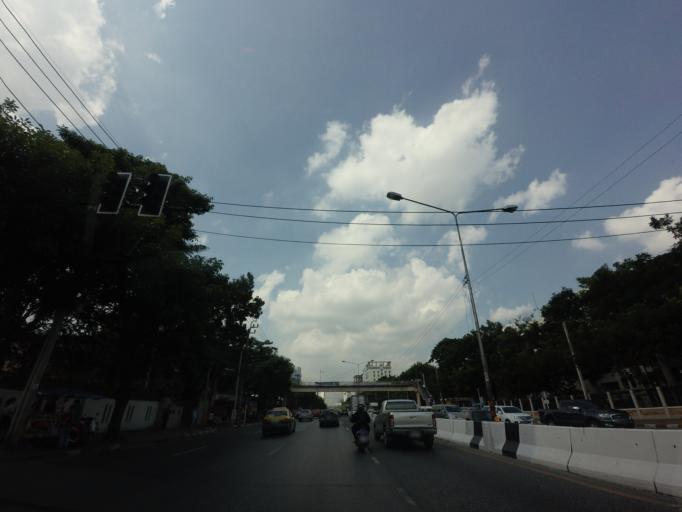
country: TH
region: Bangkok
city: Chatuchak
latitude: 13.8421
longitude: 100.5712
